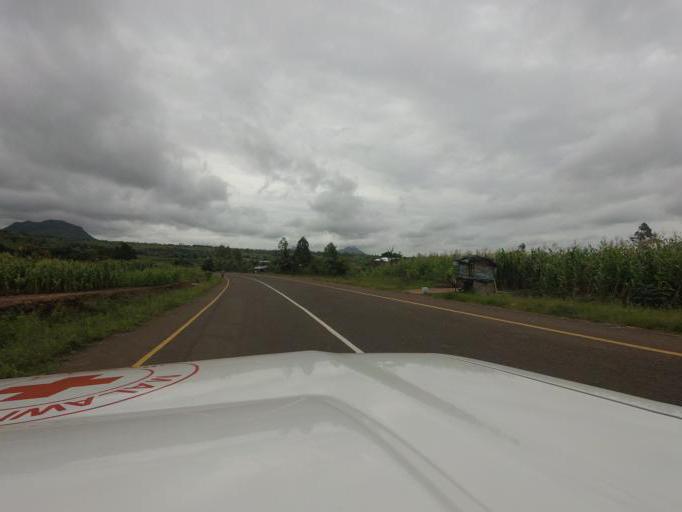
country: MW
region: Southern Region
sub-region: Thyolo District
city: Thyolo
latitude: -15.9573
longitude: 35.1902
